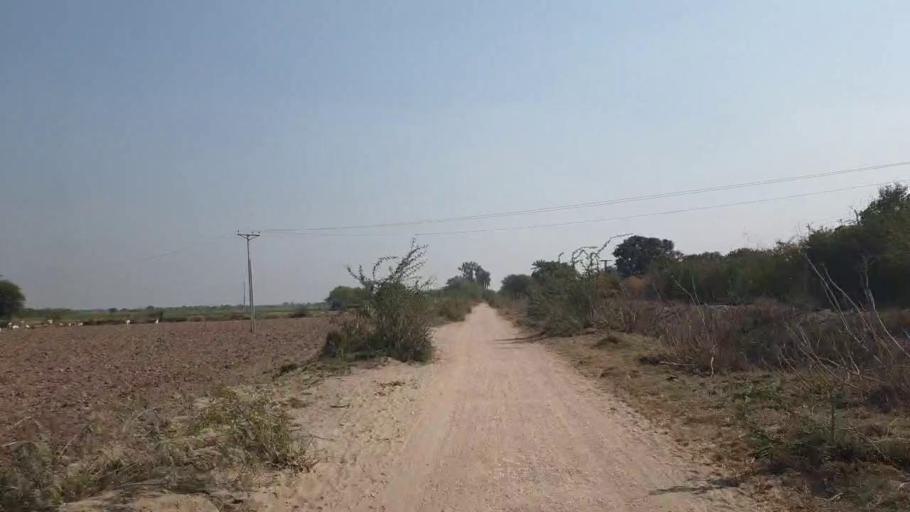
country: PK
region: Sindh
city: Chambar
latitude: 25.4083
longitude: 68.9068
